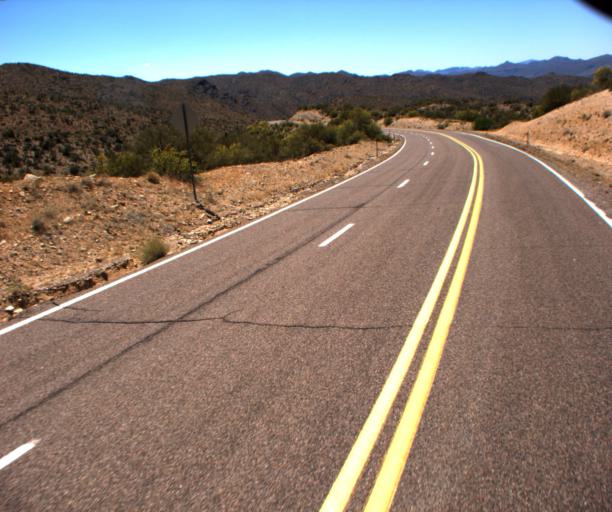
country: US
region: Arizona
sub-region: Yavapai County
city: Bagdad
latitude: 34.4613
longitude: -113.0013
